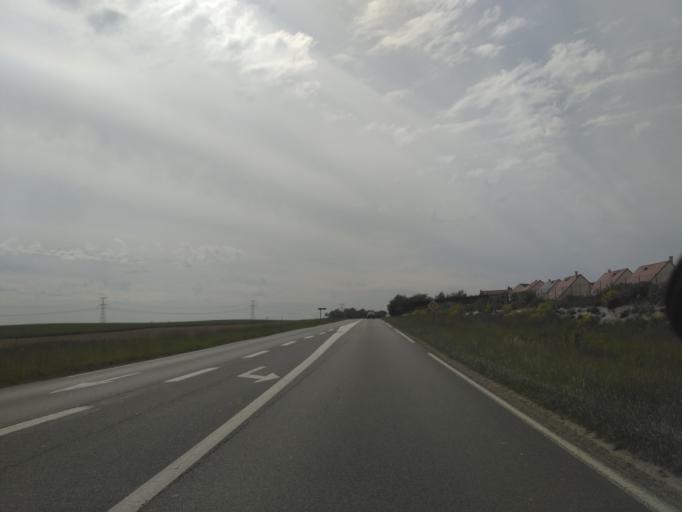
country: FR
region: Ile-de-France
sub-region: Departement de Seine-et-Marne
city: Ozouer-le-Voulgis
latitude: 48.6355
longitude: 2.7742
